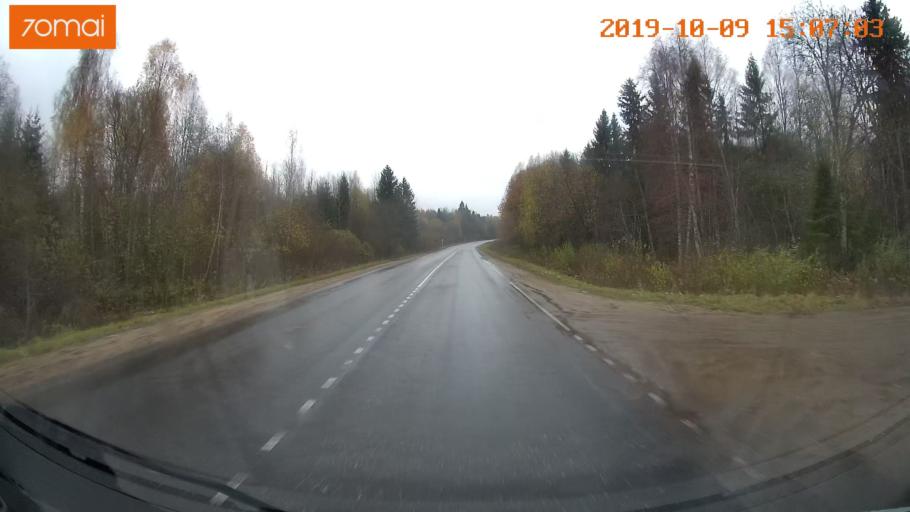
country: RU
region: Kostroma
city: Susanino
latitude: 58.2243
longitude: 41.6537
